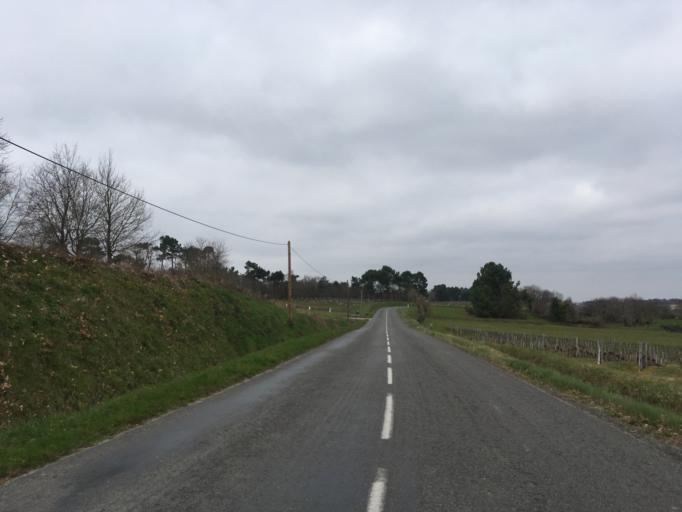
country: FR
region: Aquitaine
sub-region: Departement de la Gironde
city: Saint-Ciers-sur-Gironde
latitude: 45.3260
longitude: -0.5939
